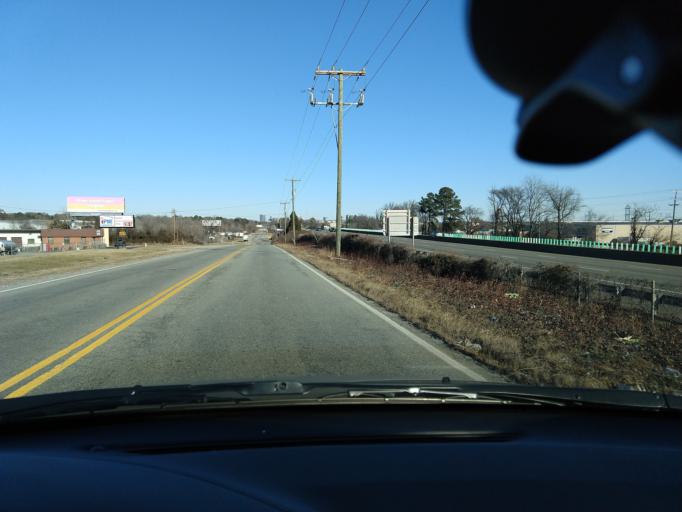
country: US
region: Virginia
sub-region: Chesterfield County
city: Bensley
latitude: 37.4877
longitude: -77.4326
